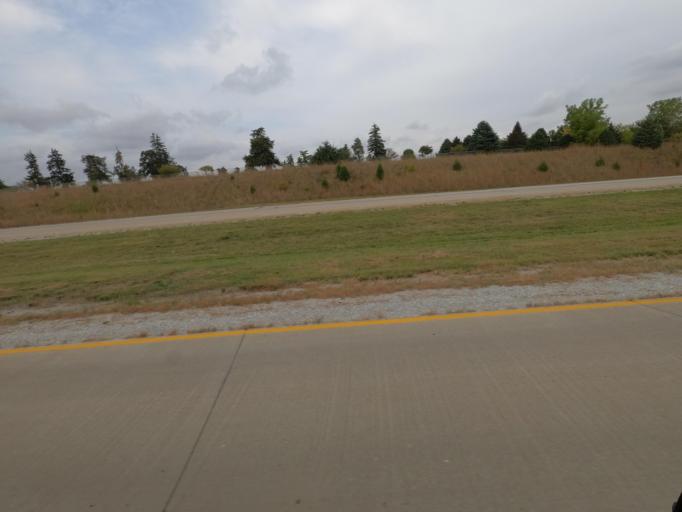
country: US
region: Iowa
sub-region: Jasper County
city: Monroe
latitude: 41.5112
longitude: -93.1068
